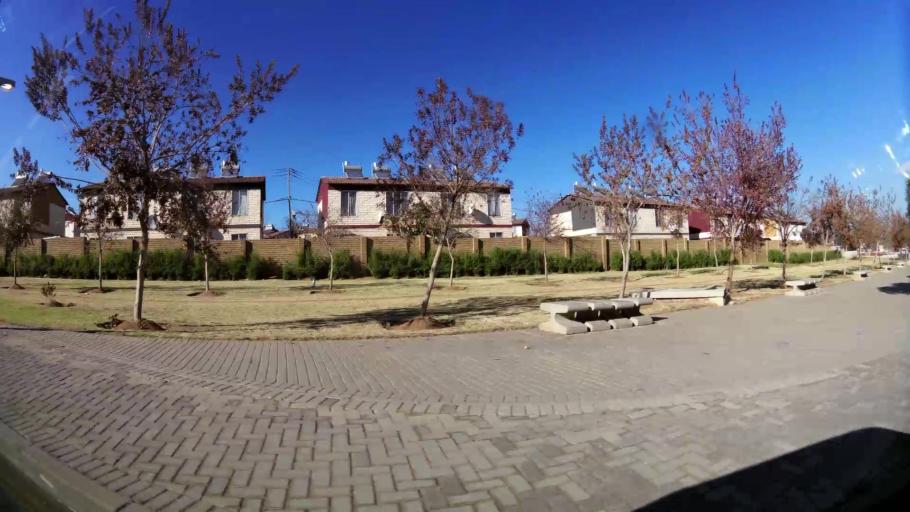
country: ZA
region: Gauteng
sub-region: City of Johannesburg Metropolitan Municipality
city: Roodepoort
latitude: -26.2160
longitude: 27.9433
